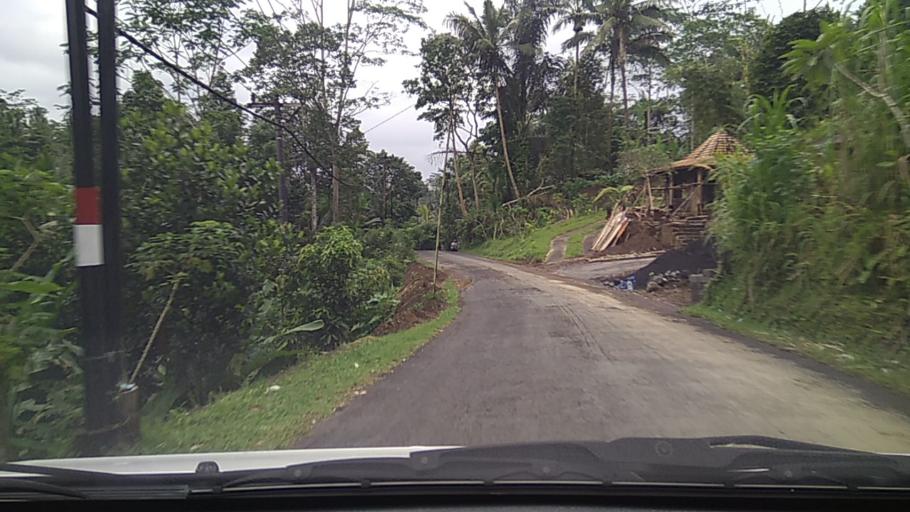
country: ID
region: Bali
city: Banjar Manukayaanyar
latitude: -8.4186
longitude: 115.3048
